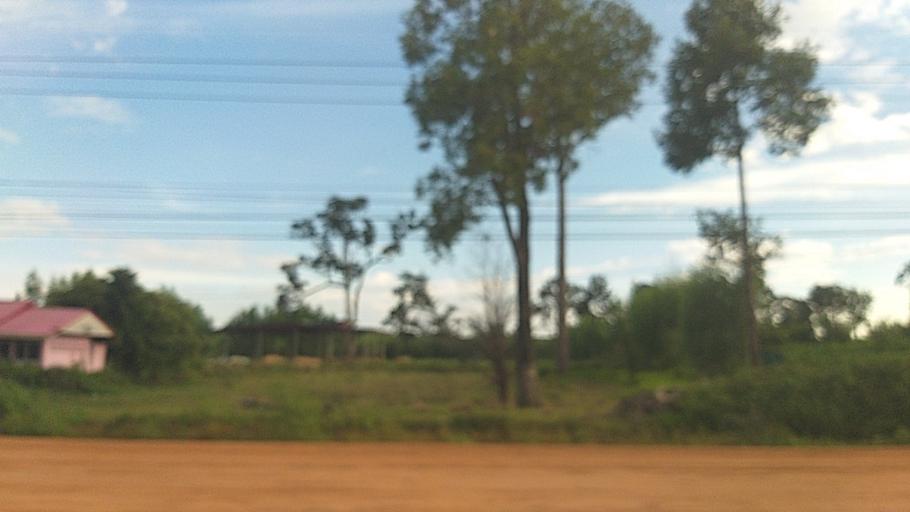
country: TH
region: Surin
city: Kap Choeng
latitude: 14.4603
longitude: 103.6605
